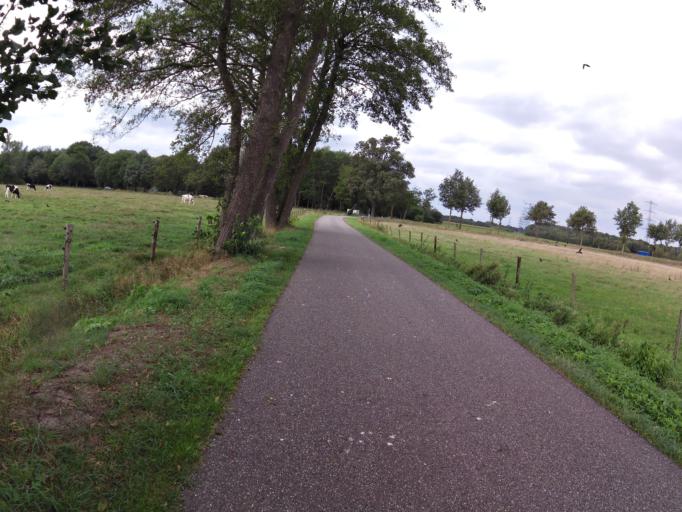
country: NL
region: Overijssel
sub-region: Gemeente Enschede
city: Enschede
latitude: 52.1939
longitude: 6.9491
